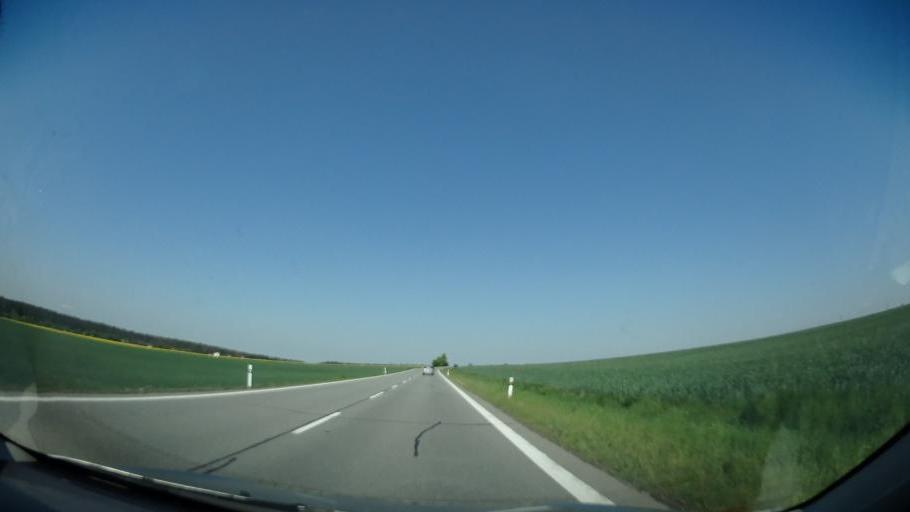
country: CZ
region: South Moravian
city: Zbraslav
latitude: 49.1857
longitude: 16.2670
